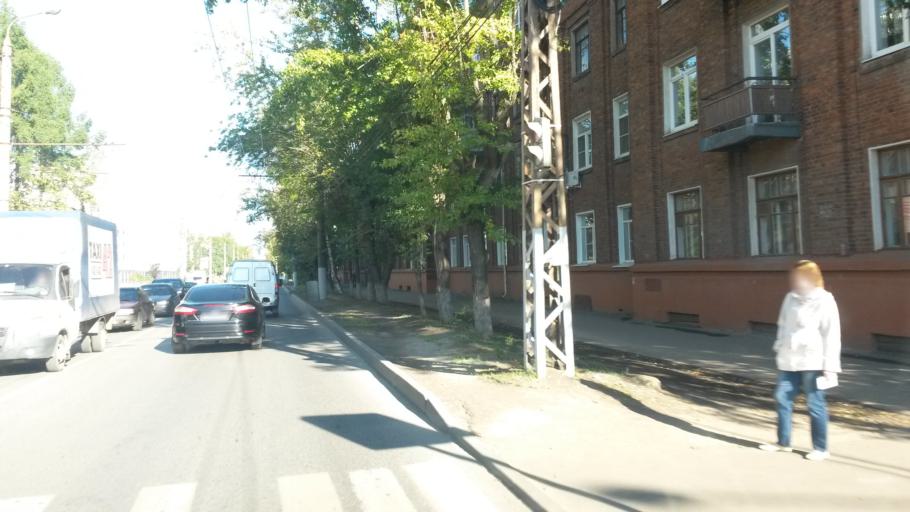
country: RU
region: Ivanovo
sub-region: Gorod Ivanovo
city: Ivanovo
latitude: 57.0015
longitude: 40.9606
